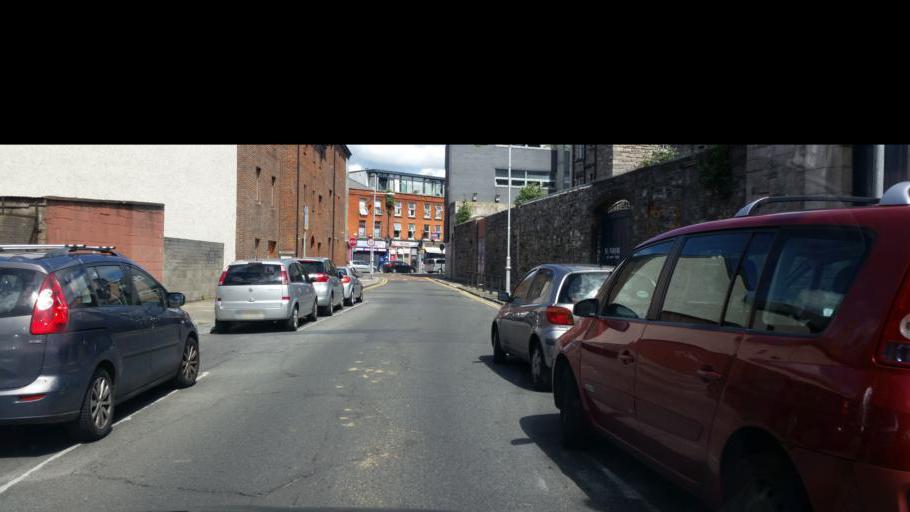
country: IE
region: Leinster
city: Drumcondra
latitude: 53.3525
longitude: -6.2687
